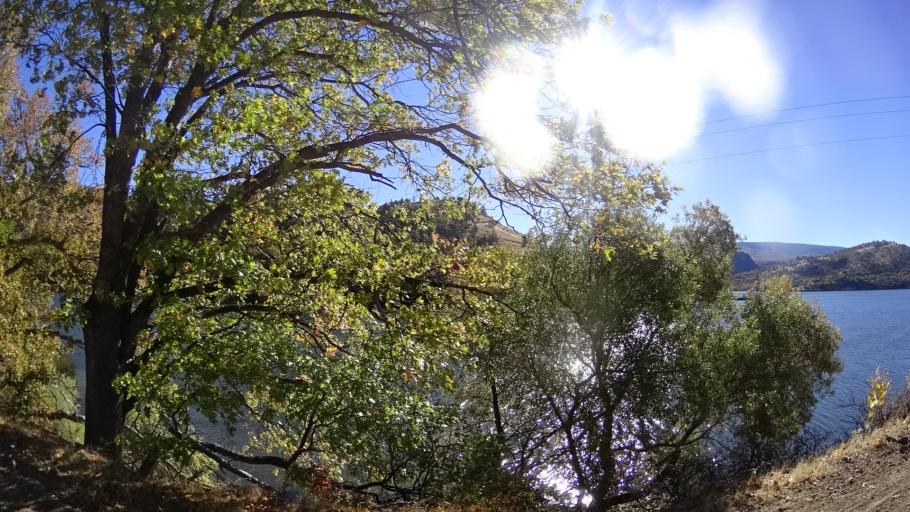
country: US
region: California
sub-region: Siskiyou County
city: Montague
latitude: 41.9918
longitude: -122.3129
